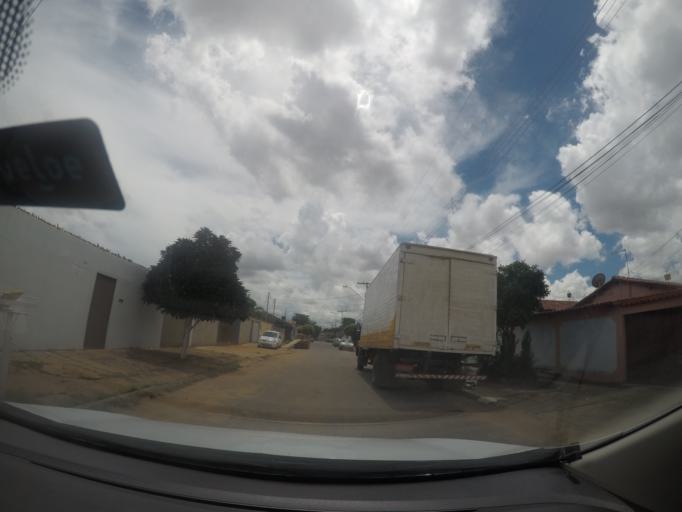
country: BR
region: Goias
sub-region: Goiania
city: Goiania
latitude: -16.6733
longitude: -49.3096
